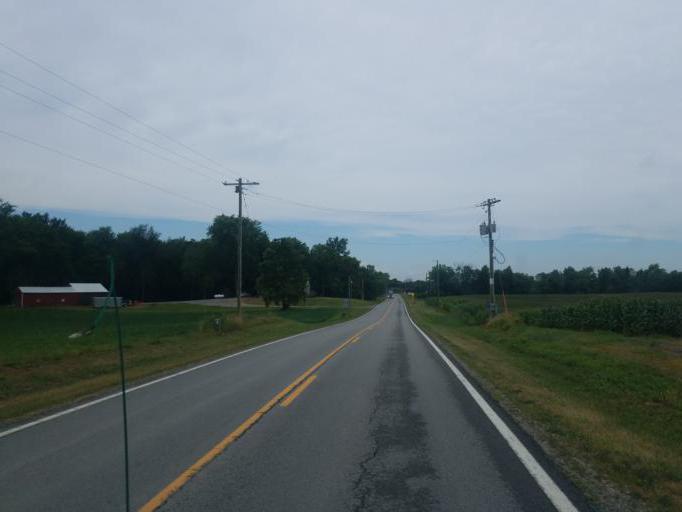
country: US
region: Ohio
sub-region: Williams County
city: Edgerton
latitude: 41.3841
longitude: -84.7978
